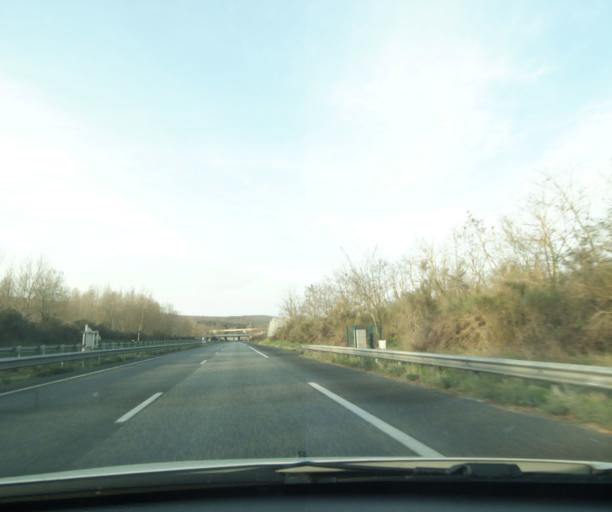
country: FR
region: Midi-Pyrenees
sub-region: Departement de la Haute-Garonne
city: Martres-Tolosane
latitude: 43.1818
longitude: 0.9796
